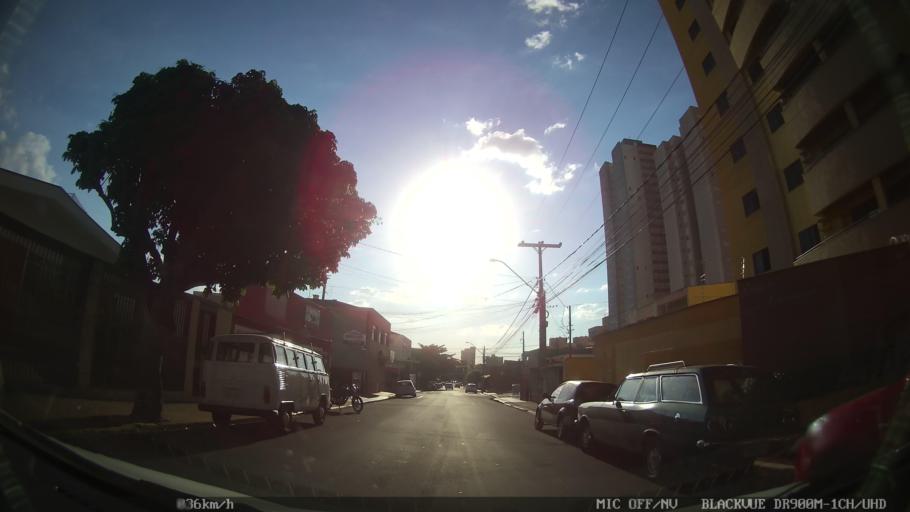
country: BR
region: Sao Paulo
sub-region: Ribeirao Preto
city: Ribeirao Preto
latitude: -21.1824
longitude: -47.7915
